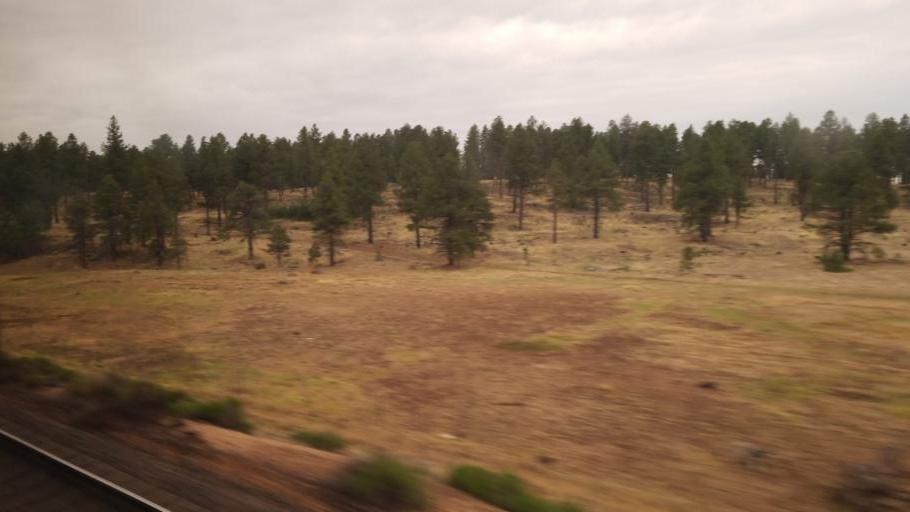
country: US
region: Arizona
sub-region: Coconino County
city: Parks
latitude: 35.2330
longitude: -112.0235
